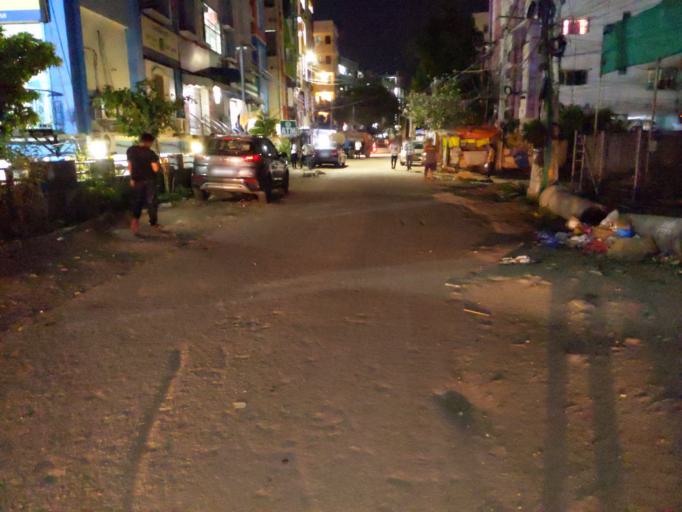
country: IN
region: Telangana
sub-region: Rangareddi
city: Kukatpalli
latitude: 17.4398
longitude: 78.3597
